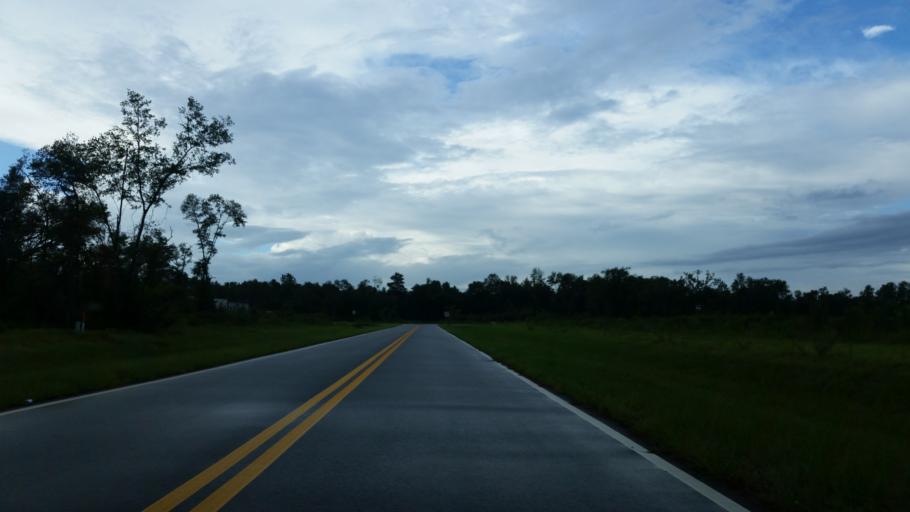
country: US
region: Florida
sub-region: Walton County
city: DeFuniak Springs
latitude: 30.7388
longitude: -86.3294
